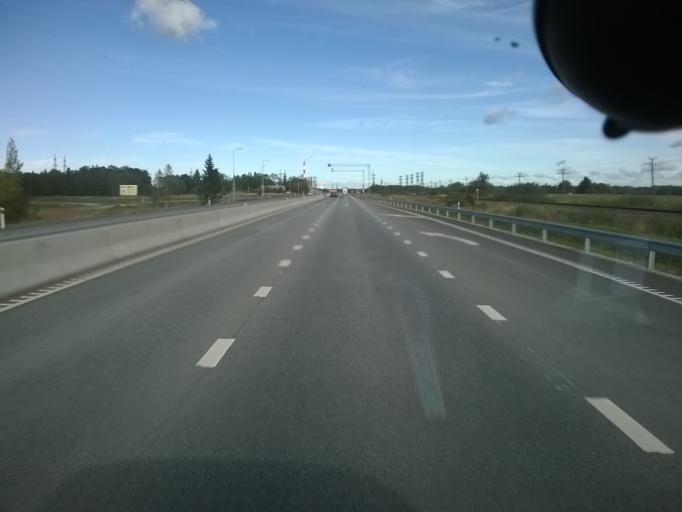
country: EE
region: Harju
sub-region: Joelaehtme vald
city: Loo
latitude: 59.4157
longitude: 24.9194
